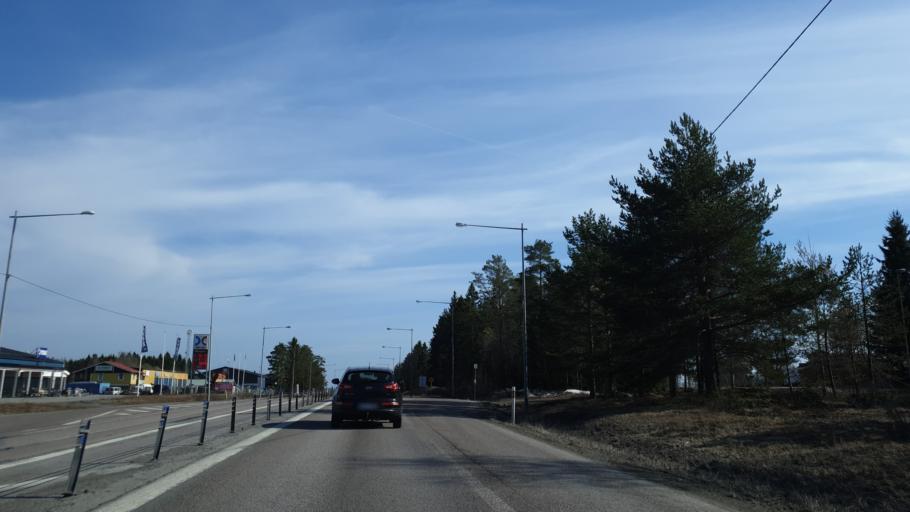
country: SE
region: Vaesternorrland
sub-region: Haernoesands Kommun
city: Haernoesand
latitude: 62.6498
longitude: 17.8934
